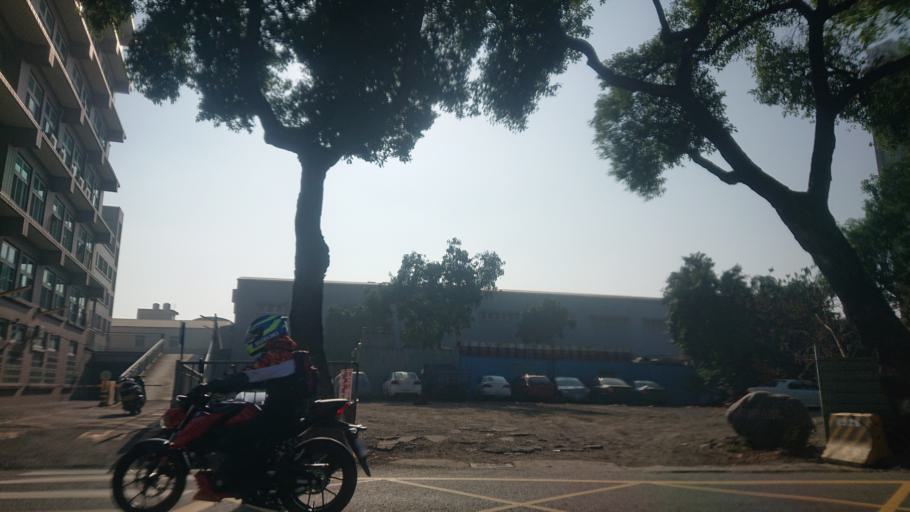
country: TW
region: Taiwan
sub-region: Tainan
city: Tainan
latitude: 23.0168
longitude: 120.2380
